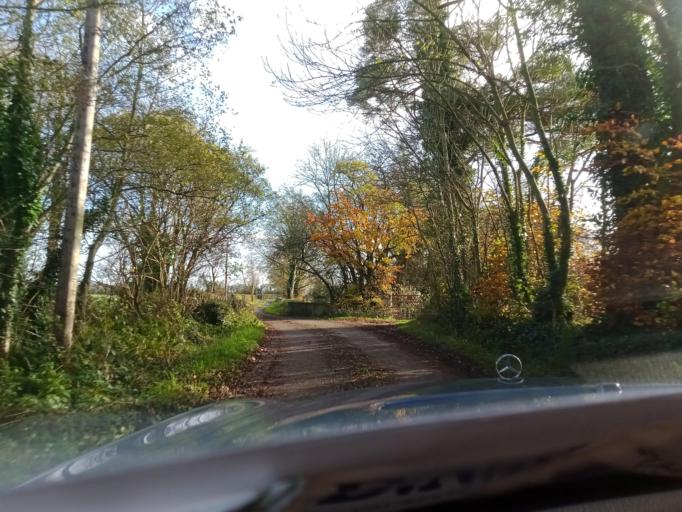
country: IE
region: Leinster
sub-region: Kilkenny
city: Mooncoin
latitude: 52.3279
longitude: -7.2758
